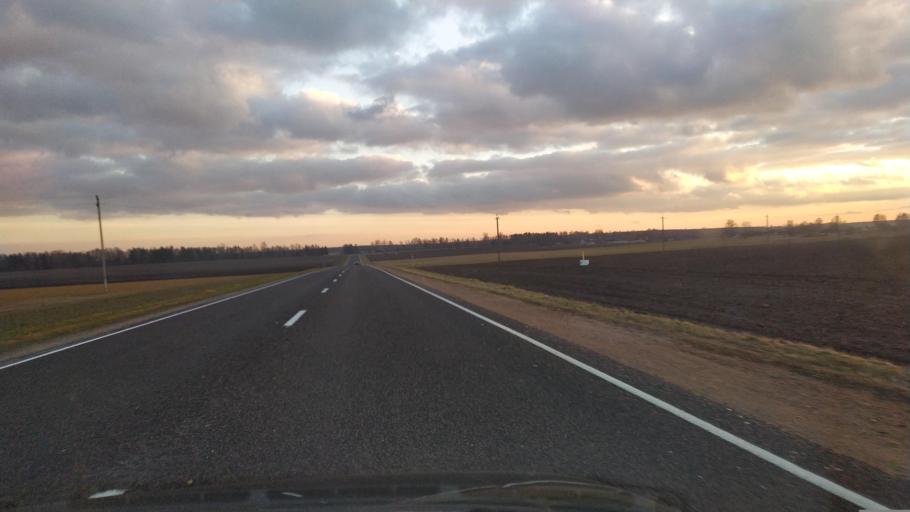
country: BY
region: Brest
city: Kamyanyets
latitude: 52.3797
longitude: 23.7893
